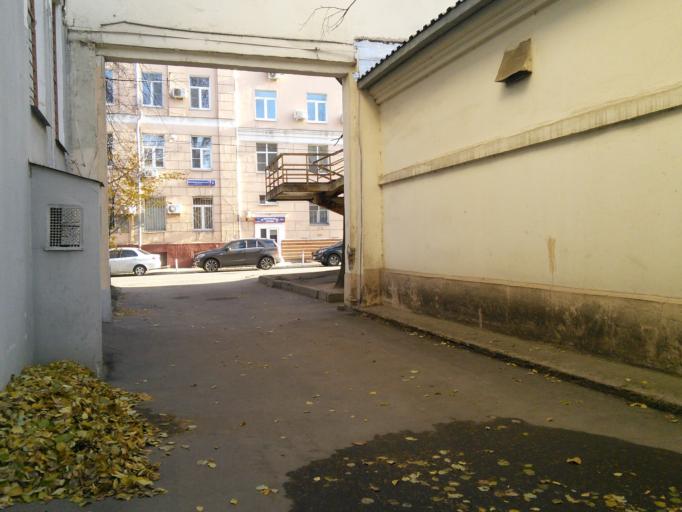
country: RU
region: Moskovskaya
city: Dorogomilovo
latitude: 55.7595
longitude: 37.5711
